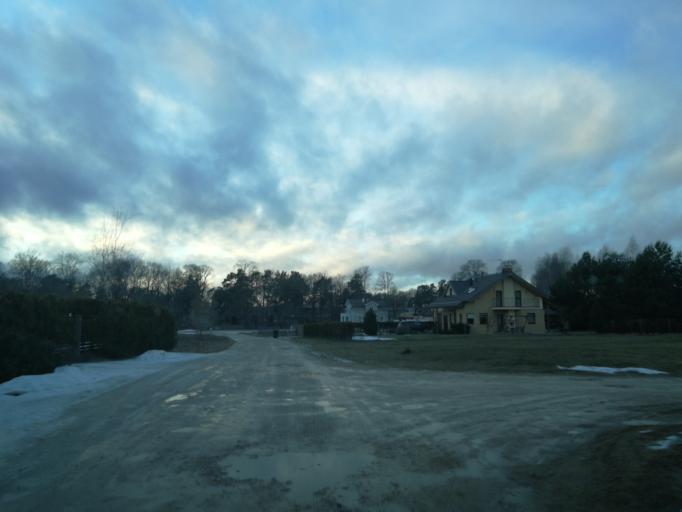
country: LV
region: Adazi
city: Adazi
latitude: 57.0746
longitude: 24.3467
